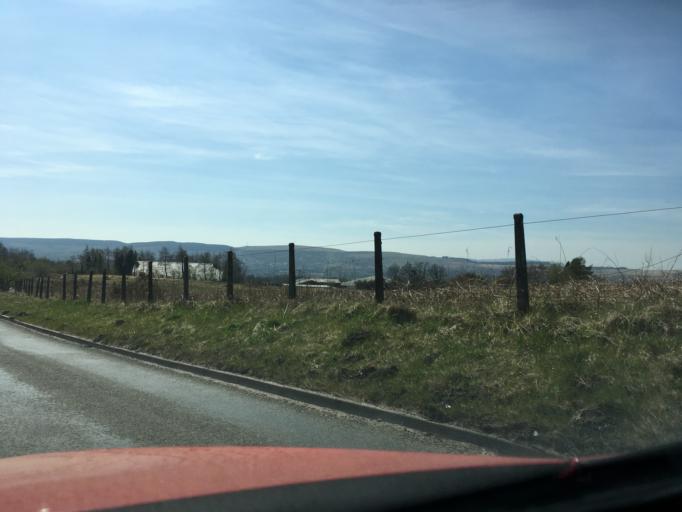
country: GB
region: Wales
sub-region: Merthyr Tydfil County Borough
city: Merthyr Tydfil
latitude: 51.7692
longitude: -3.3691
